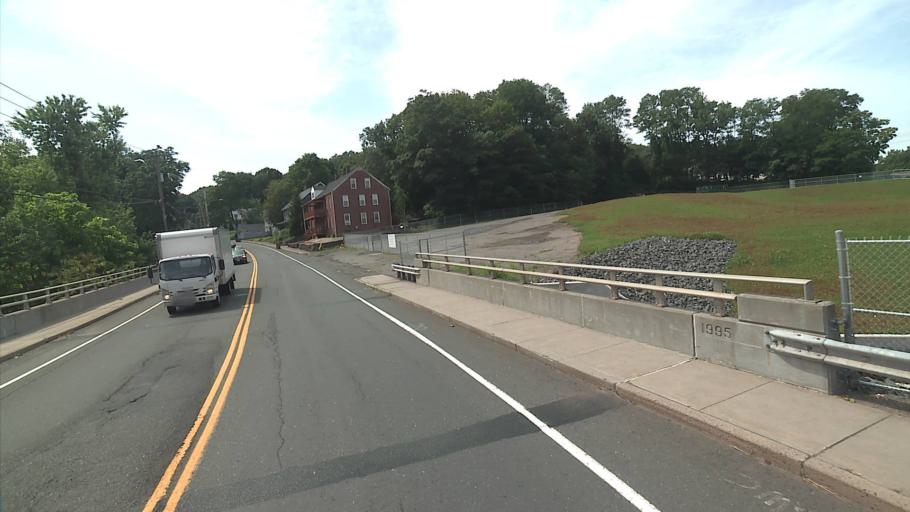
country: US
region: Connecticut
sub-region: Tolland County
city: Rockville
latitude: 41.8670
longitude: -72.4424
